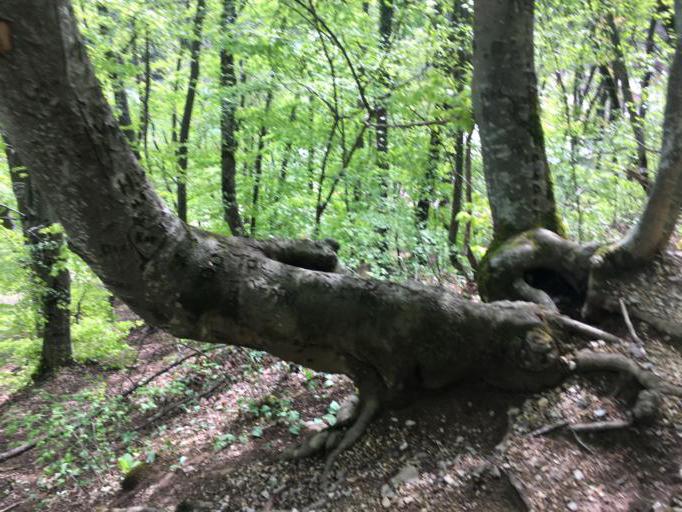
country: XK
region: Pristina
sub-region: Komuna e Prishtines
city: Pristina
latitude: 42.6698
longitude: 21.2172
